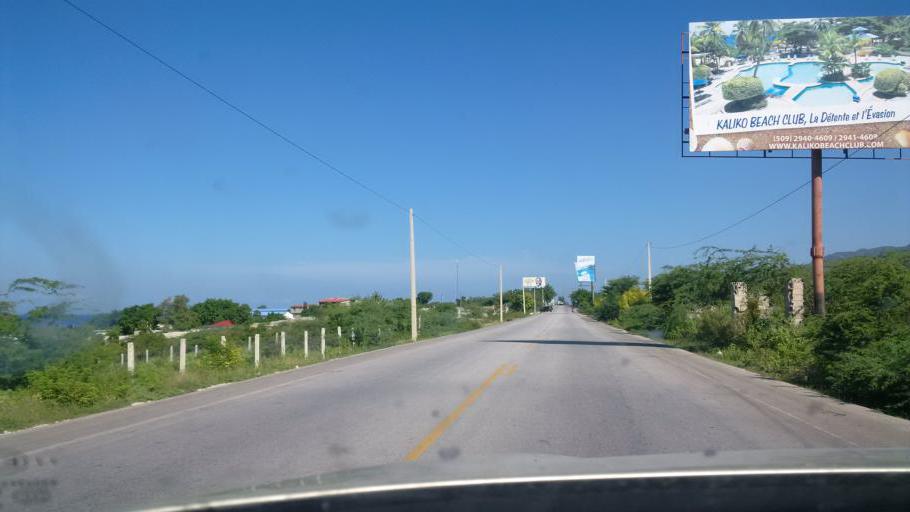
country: HT
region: Ouest
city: Cabaret
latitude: 18.8675
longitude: -72.6059
